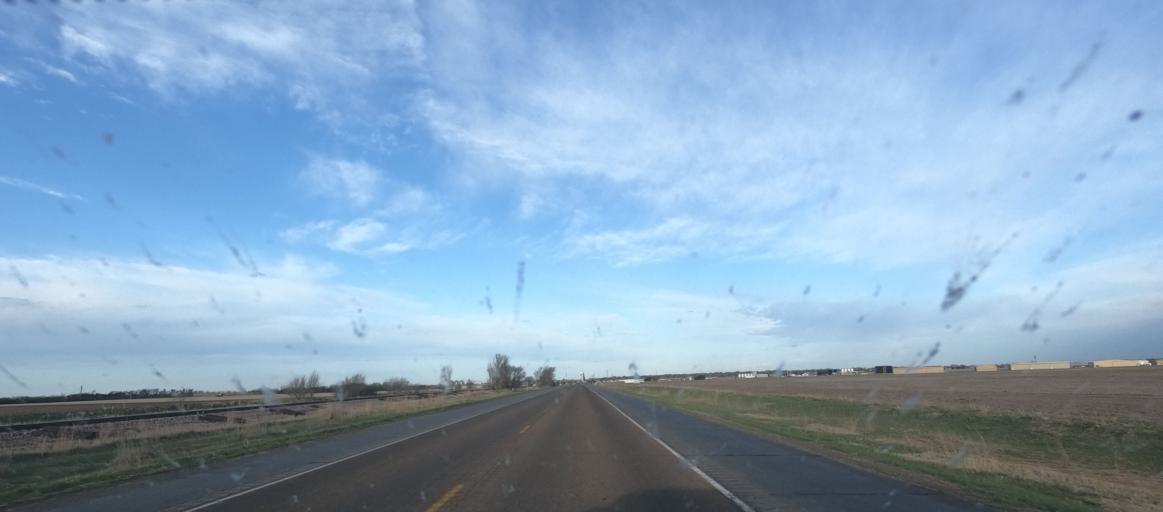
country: US
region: Nebraska
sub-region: Phelps County
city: Holdrege
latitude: 40.4451
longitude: -99.3306
